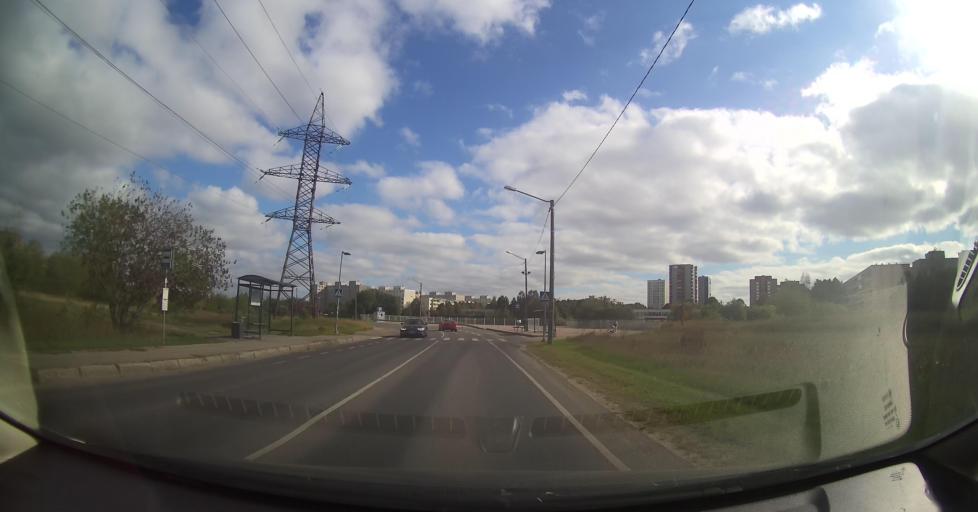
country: EE
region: Harju
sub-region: Tallinna linn
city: Kose
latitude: 59.4451
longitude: 24.8370
